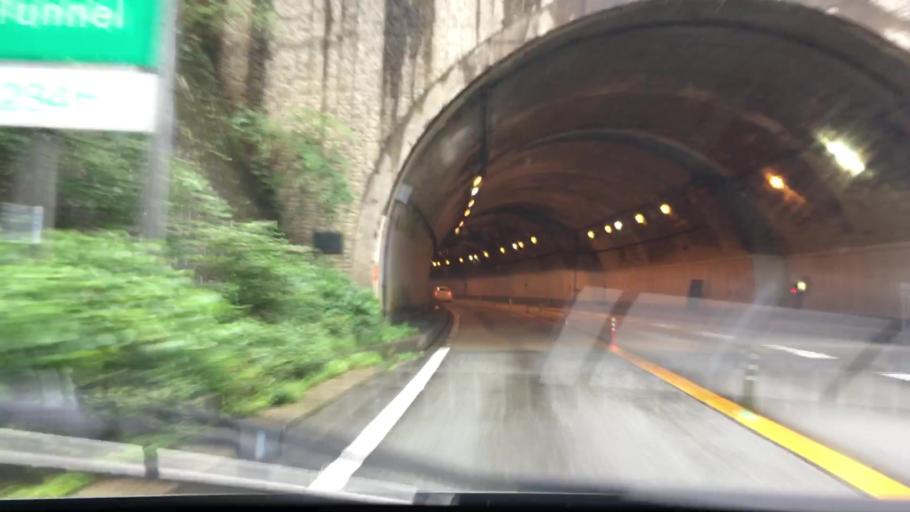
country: JP
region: Hyogo
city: Nishiwaki
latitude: 35.1624
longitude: 134.7851
